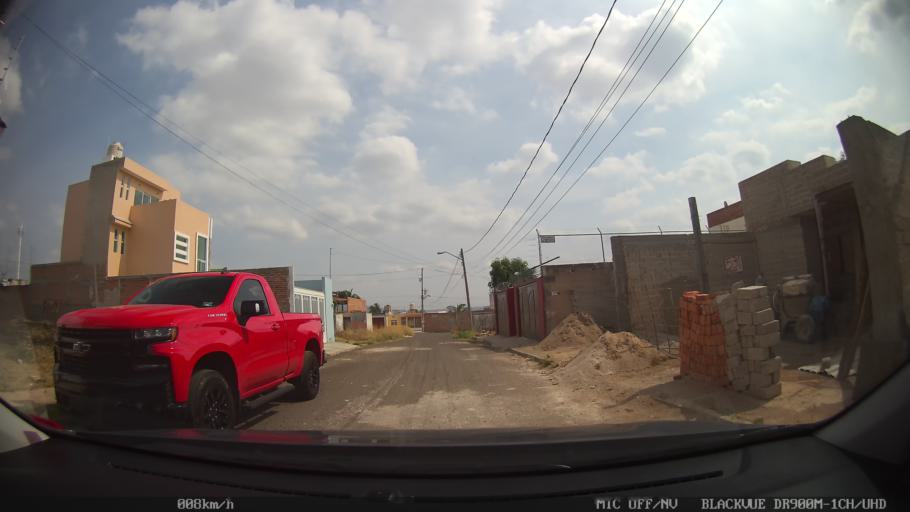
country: MX
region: Jalisco
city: Coyula
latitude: 20.6379
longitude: -103.2162
